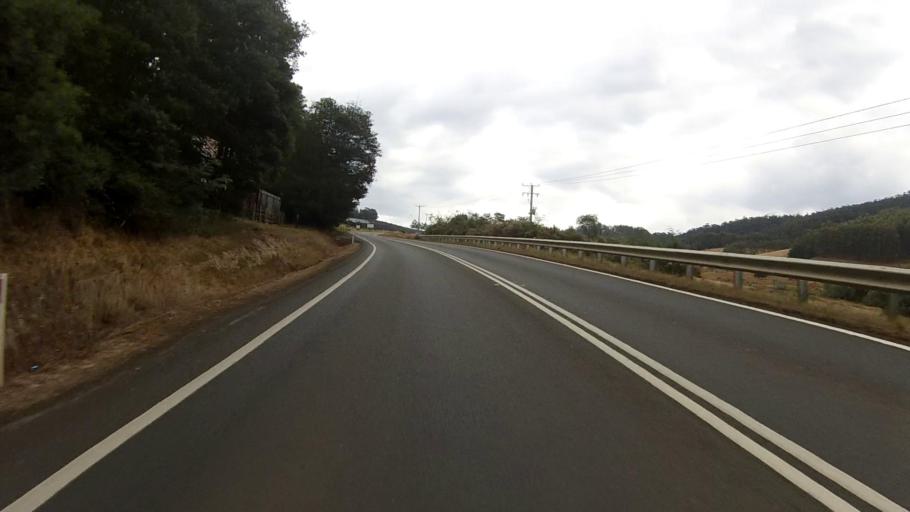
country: AU
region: Tasmania
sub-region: Huon Valley
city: Cygnet
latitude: -43.1349
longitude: 147.0533
